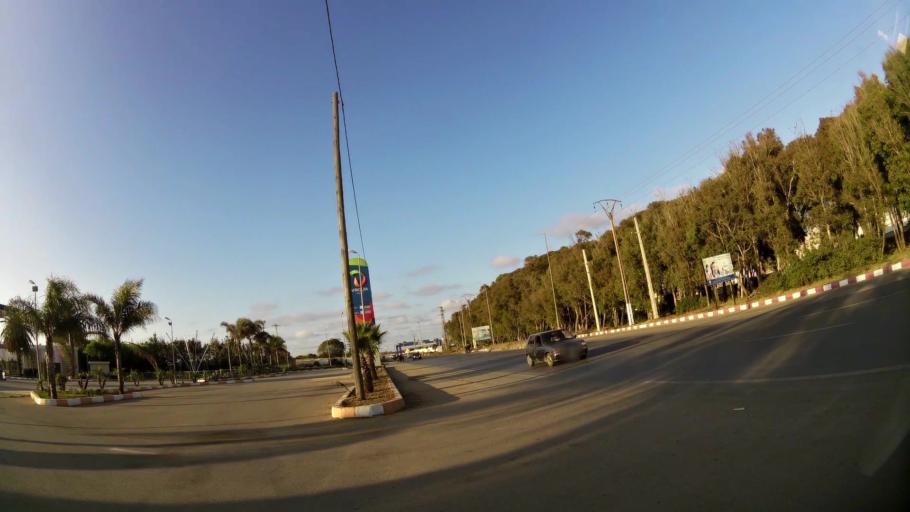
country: MA
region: Rabat-Sale-Zemmour-Zaer
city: Sale
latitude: 34.1143
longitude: -6.7467
